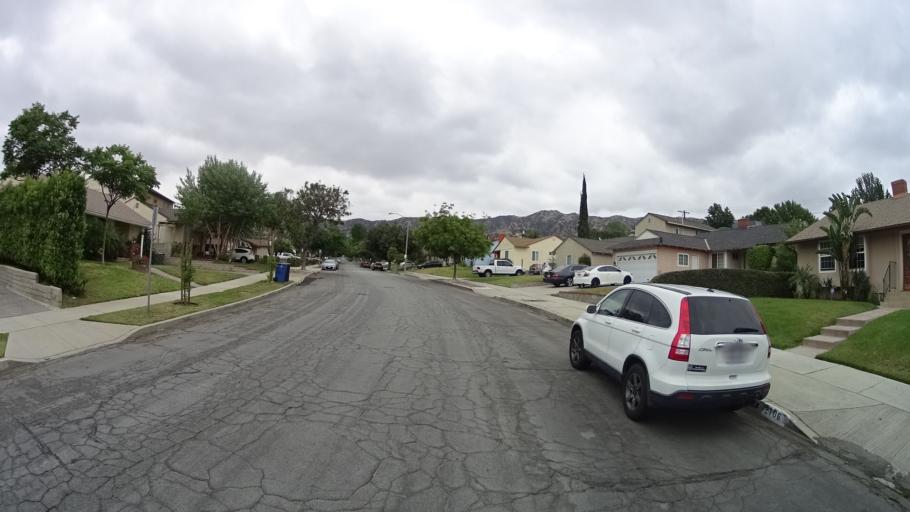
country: US
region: California
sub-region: Los Angeles County
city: Burbank
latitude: 34.2047
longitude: -118.3366
